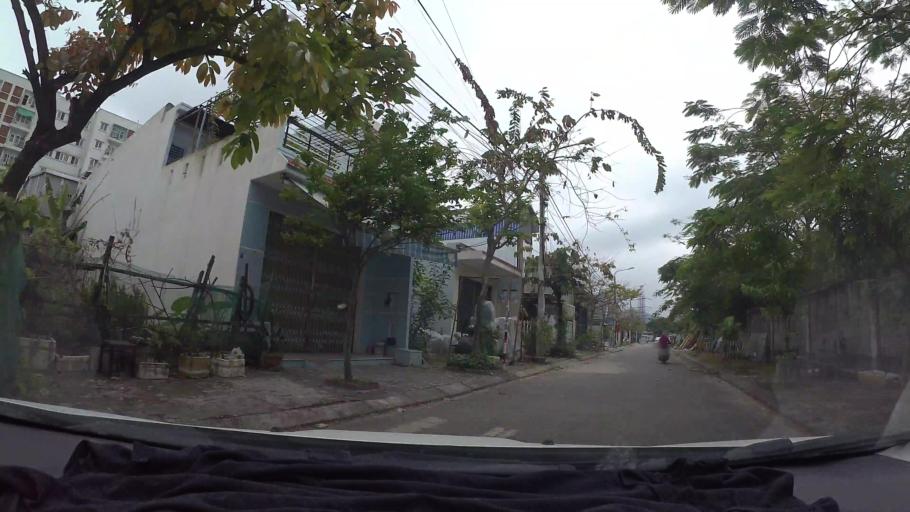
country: VN
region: Da Nang
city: Thanh Khe
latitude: 16.0458
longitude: 108.1742
